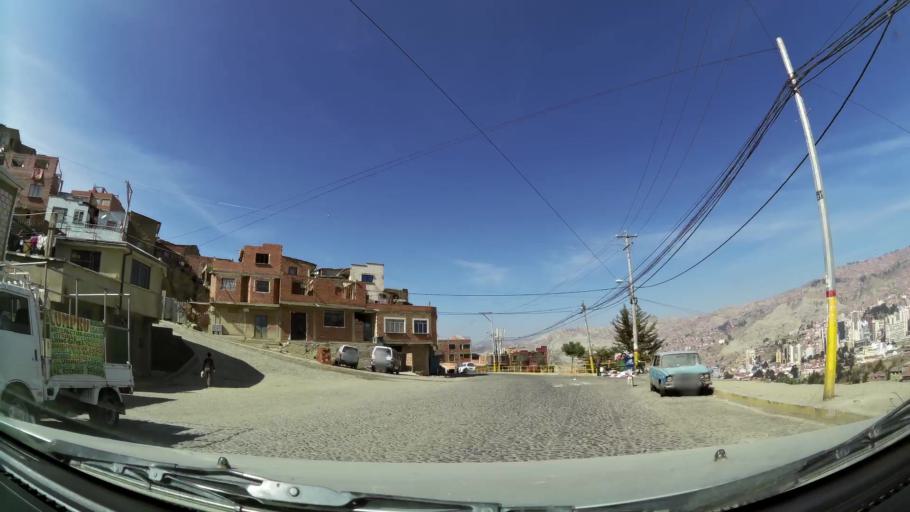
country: BO
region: La Paz
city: La Paz
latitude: -16.5035
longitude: -68.1111
